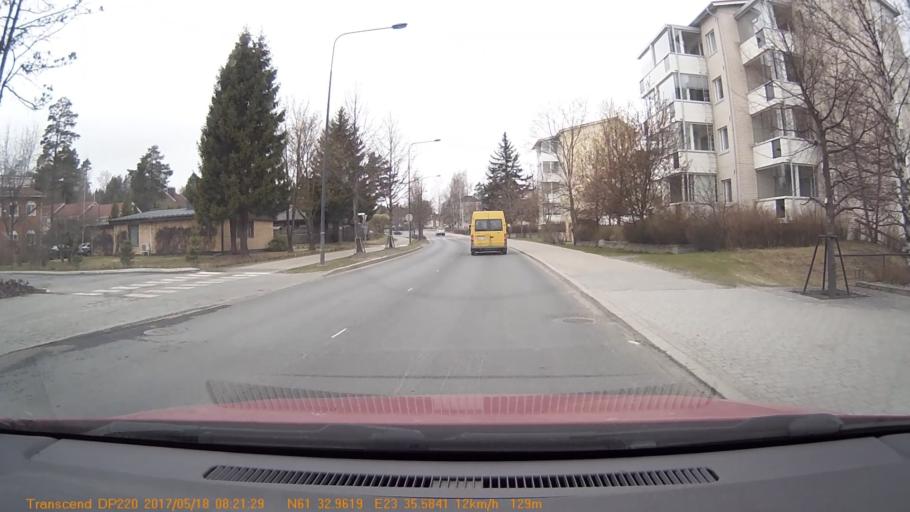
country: FI
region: Pirkanmaa
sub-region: Tampere
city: Yloejaervi
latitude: 61.5493
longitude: 23.5933
